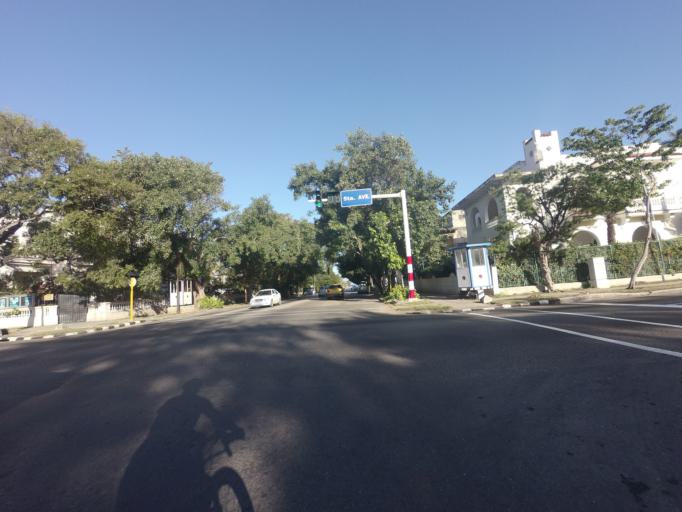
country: CU
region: La Habana
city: Havana
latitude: 23.1194
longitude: -82.4246
